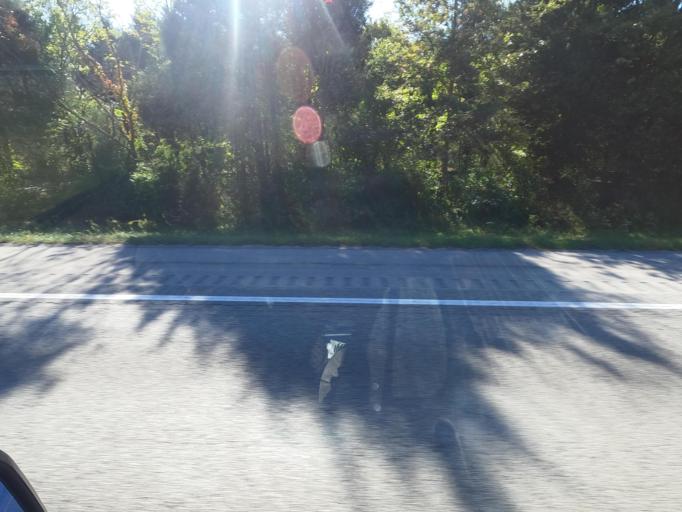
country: US
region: Tennessee
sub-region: Marion County
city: Kimball
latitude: 35.1044
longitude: -85.7410
